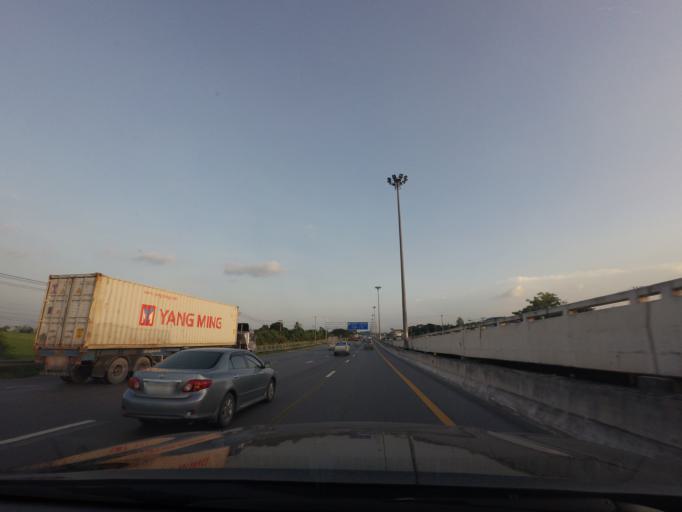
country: TH
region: Pathum Thani
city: Khlong Luang
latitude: 14.0984
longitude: 100.6881
